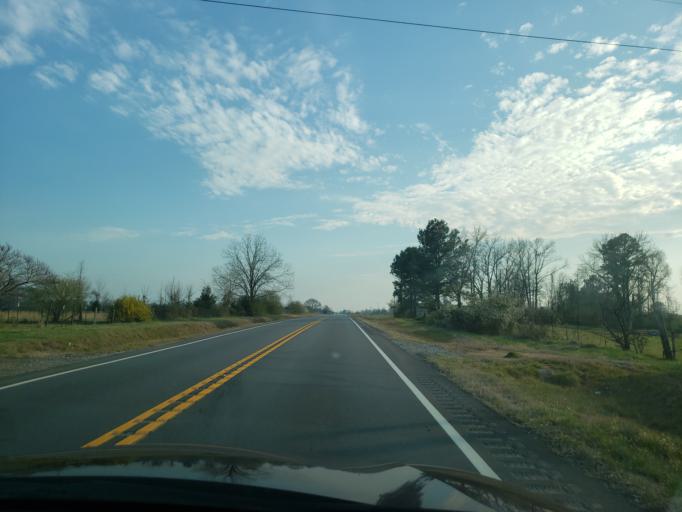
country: US
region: Alabama
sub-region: Hale County
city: Moundville
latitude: 32.8785
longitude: -87.6095
